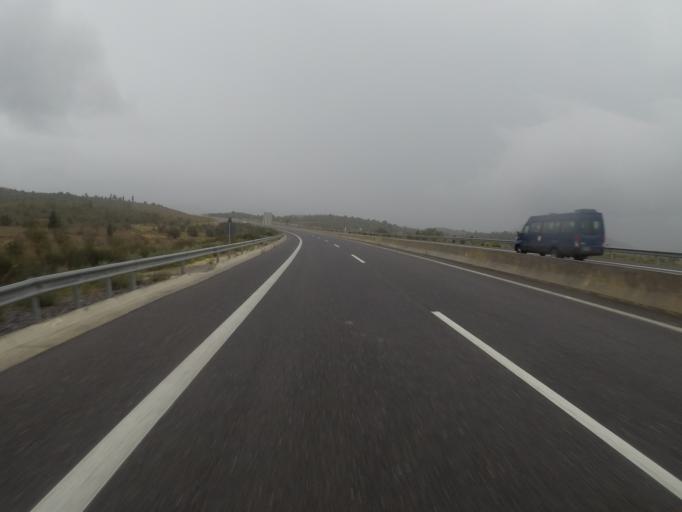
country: GR
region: Peloponnese
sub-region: Nomos Arkadias
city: Megalopoli
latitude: 37.3868
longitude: 22.2698
